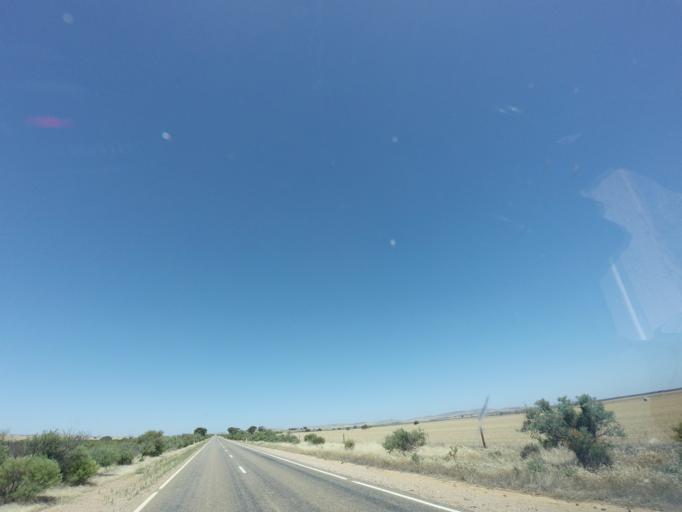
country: AU
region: South Australia
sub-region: Flinders Ranges
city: Quorn
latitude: -32.6998
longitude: 138.3879
